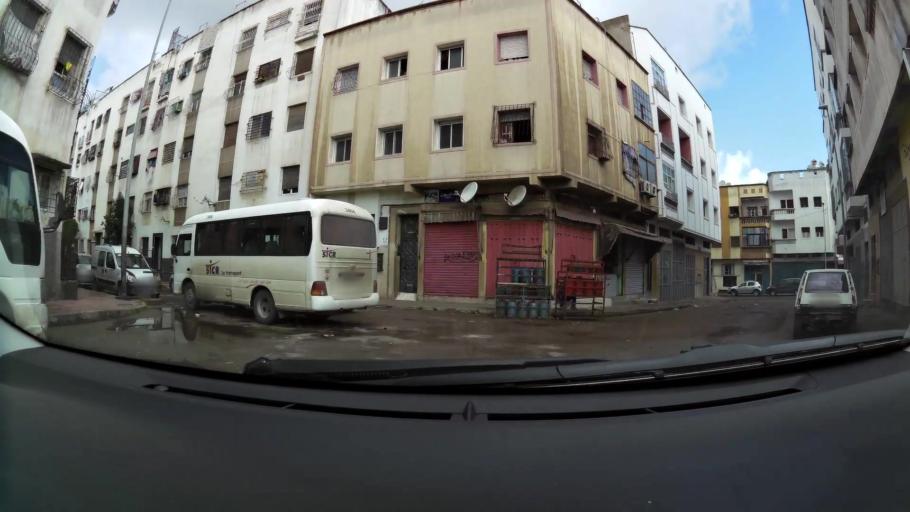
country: MA
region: Grand Casablanca
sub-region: Mediouna
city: Tit Mellil
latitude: 33.5937
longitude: -7.5165
